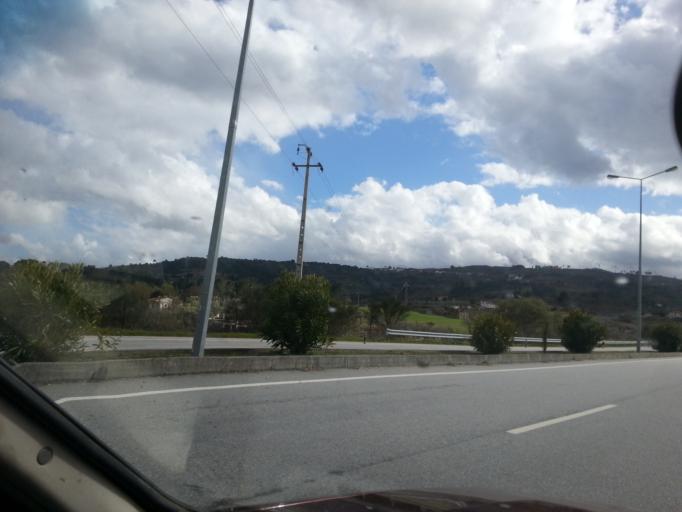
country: PT
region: Guarda
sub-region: Celorico da Beira
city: Celorico da Beira
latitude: 40.6364
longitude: -7.3844
